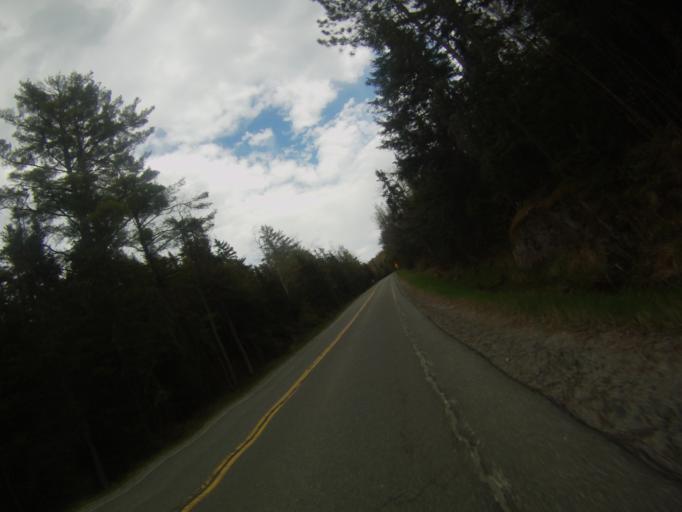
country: US
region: New York
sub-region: Essex County
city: Mineville
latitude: 44.0999
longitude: -73.5671
